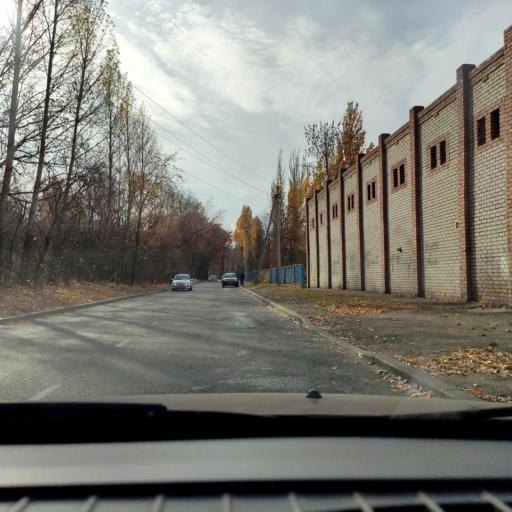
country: RU
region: Samara
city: Tol'yatti
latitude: 53.5223
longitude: 49.3336
